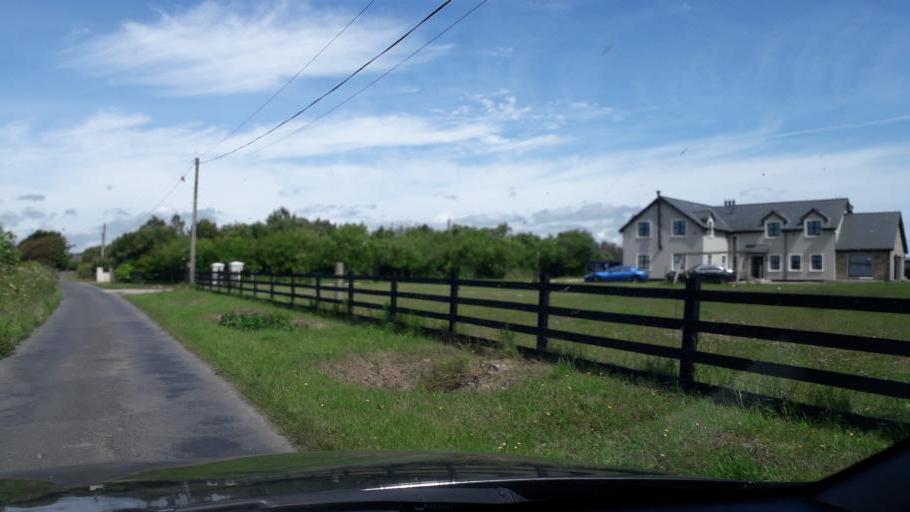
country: IE
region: Leinster
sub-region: Loch Garman
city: Loch Garman
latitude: 52.1897
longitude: -6.5438
